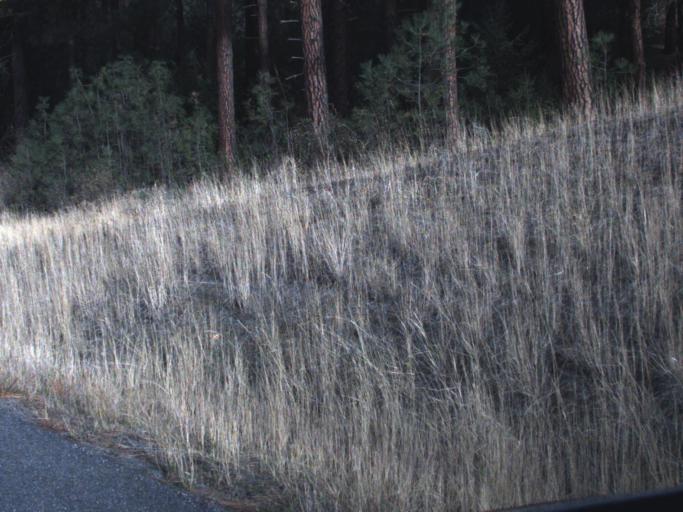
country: US
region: Washington
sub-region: Stevens County
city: Kettle Falls
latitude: 48.5230
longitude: -118.1387
